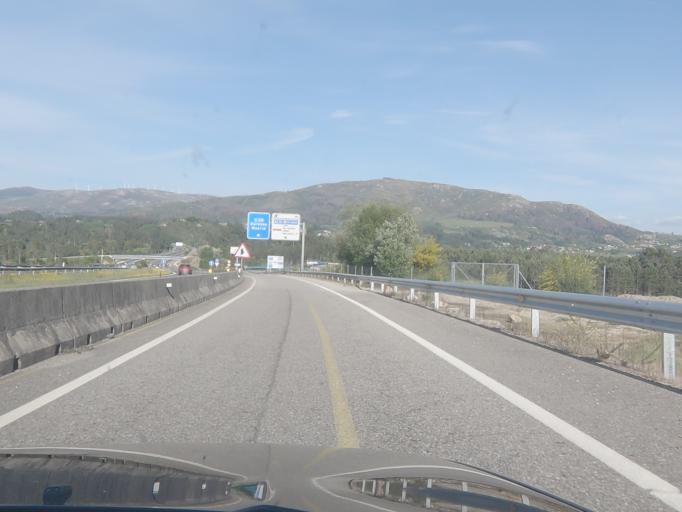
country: ES
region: Galicia
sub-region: Provincia de Pontevedra
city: Ponteareas
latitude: 42.1424
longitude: -8.4687
